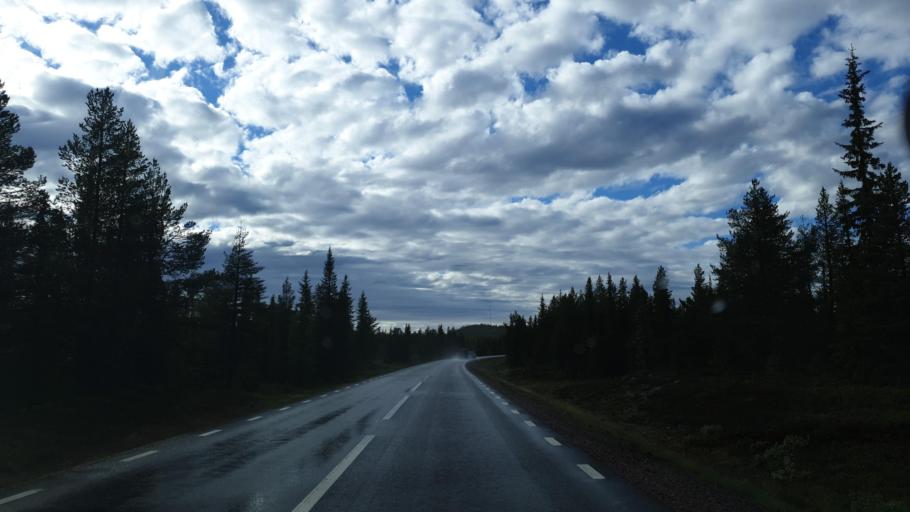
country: SE
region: Norrbotten
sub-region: Arjeplogs Kommun
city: Arjeplog
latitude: 65.8908
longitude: 18.3741
